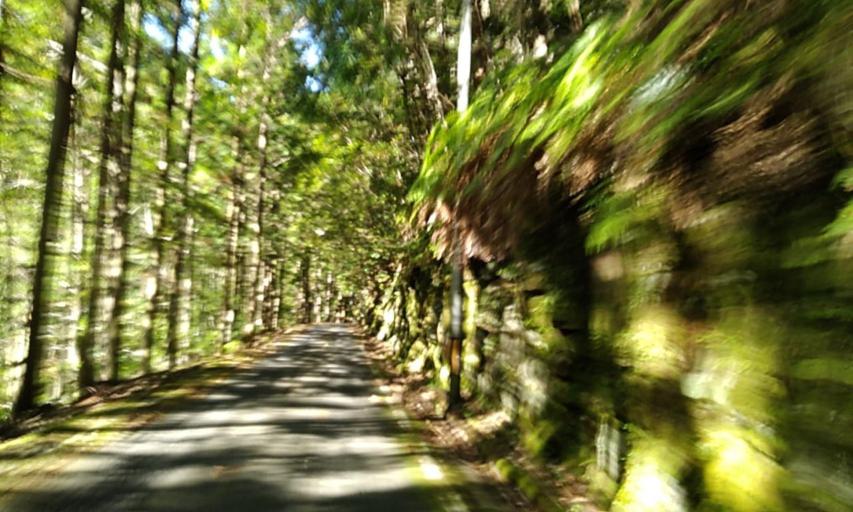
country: JP
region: Wakayama
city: Shingu
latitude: 33.9086
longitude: 135.9988
